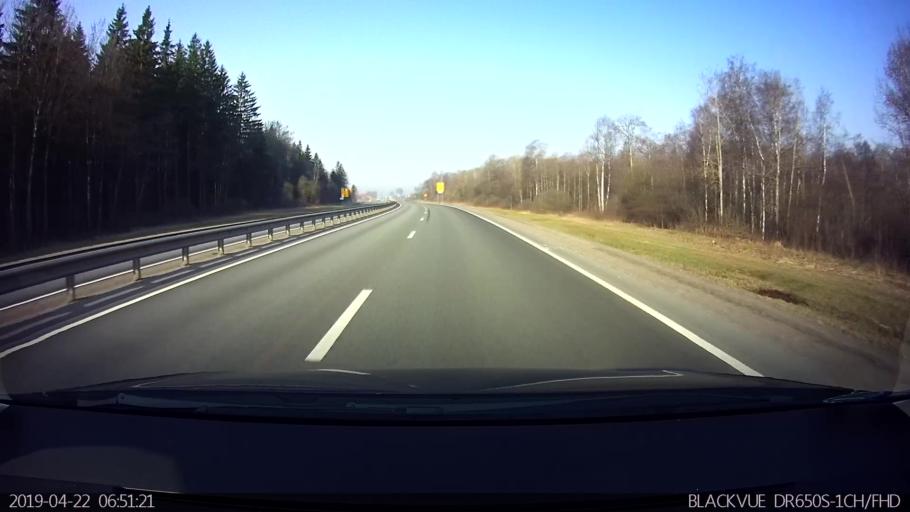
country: RU
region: Smolensk
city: Gagarin
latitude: 55.4933
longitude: 34.9775
